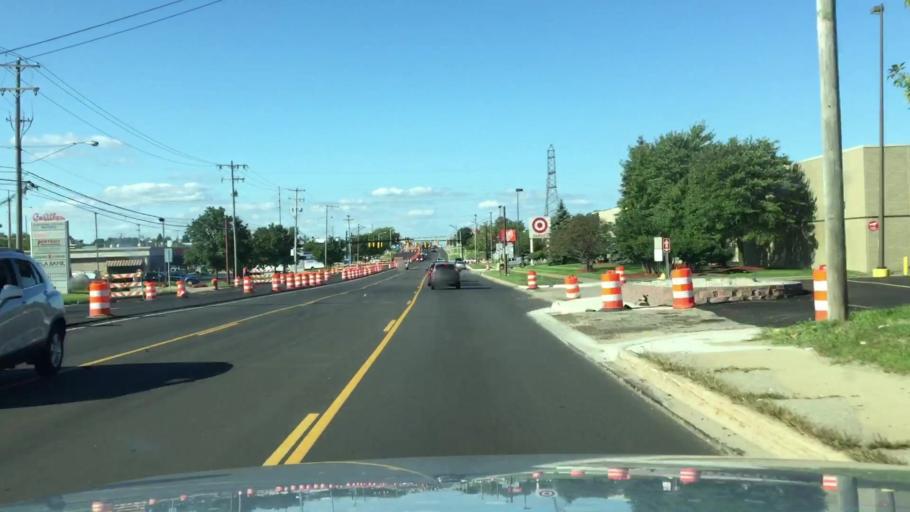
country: US
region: Michigan
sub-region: Kalamazoo County
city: Portage
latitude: 42.2172
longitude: -85.5893
